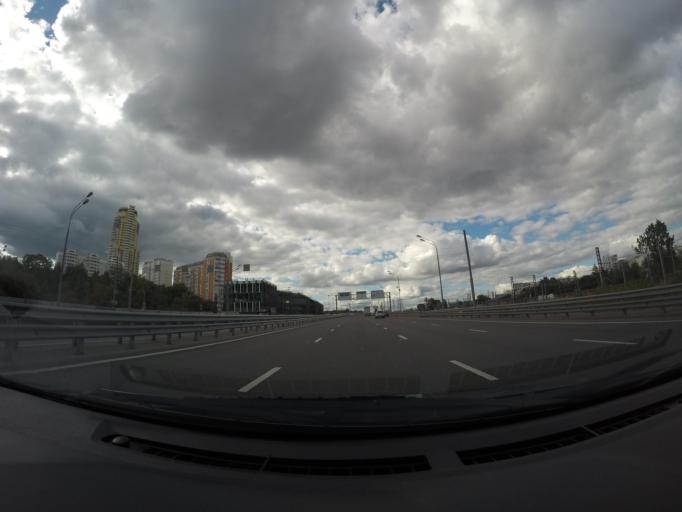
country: RU
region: Moskovskaya
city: Levoberezhnaya
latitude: 55.8772
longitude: 37.4908
